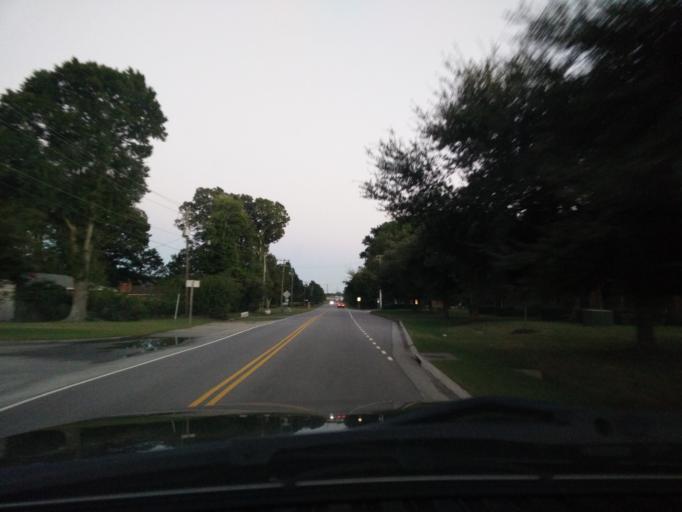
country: US
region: Virginia
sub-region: City of Chesapeake
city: Chesapeake
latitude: 36.7493
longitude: -76.2353
